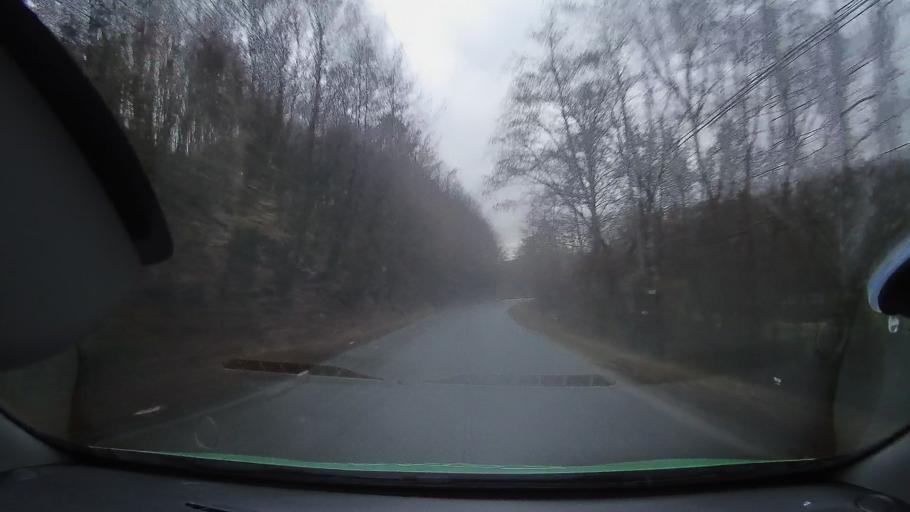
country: RO
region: Hunedoara
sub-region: Comuna Baia de Cris
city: Baia de Cris
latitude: 46.1964
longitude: 22.7173
